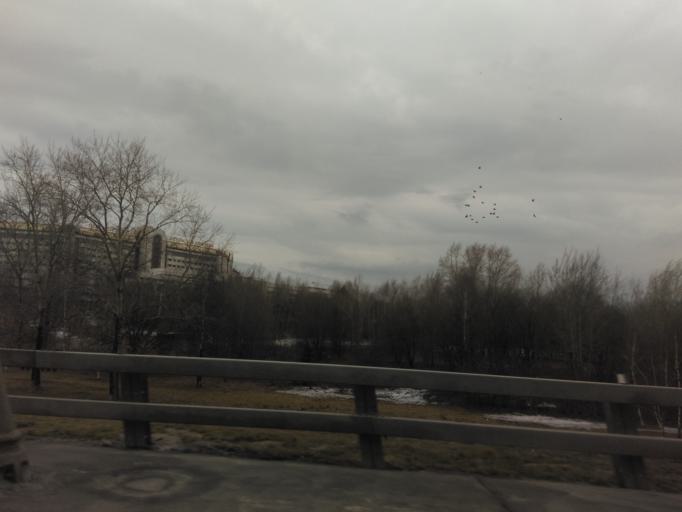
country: RU
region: Moscow
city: Rublevo
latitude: 55.7655
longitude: 37.3784
